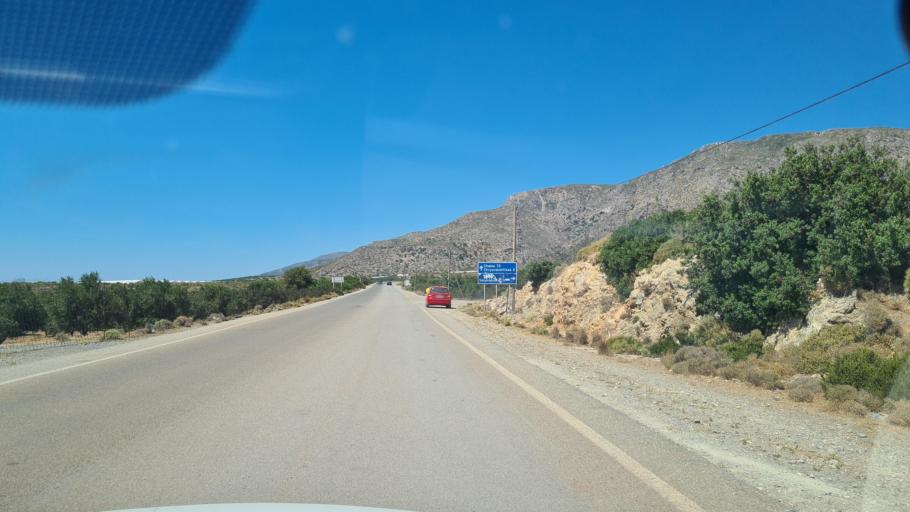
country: GR
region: Crete
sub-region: Nomos Chanias
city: Palaiochora
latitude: 35.2828
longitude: 23.5476
